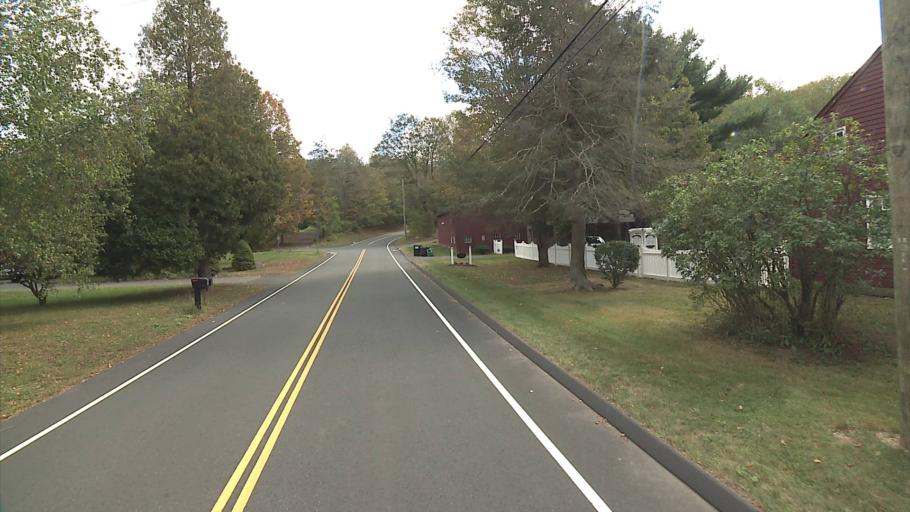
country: US
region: Connecticut
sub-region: Middlesex County
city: Durham
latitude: 41.4361
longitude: -72.6458
